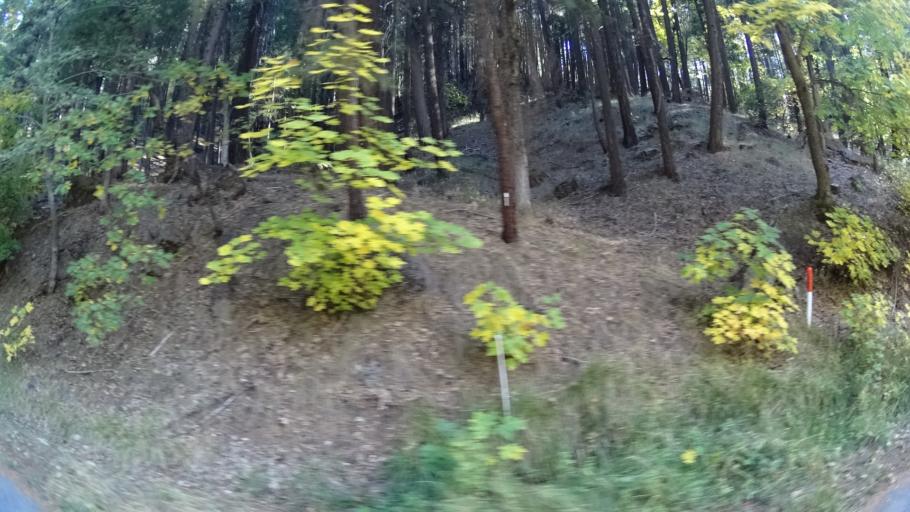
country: US
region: California
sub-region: Siskiyou County
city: Happy Camp
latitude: 41.6376
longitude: -123.1072
